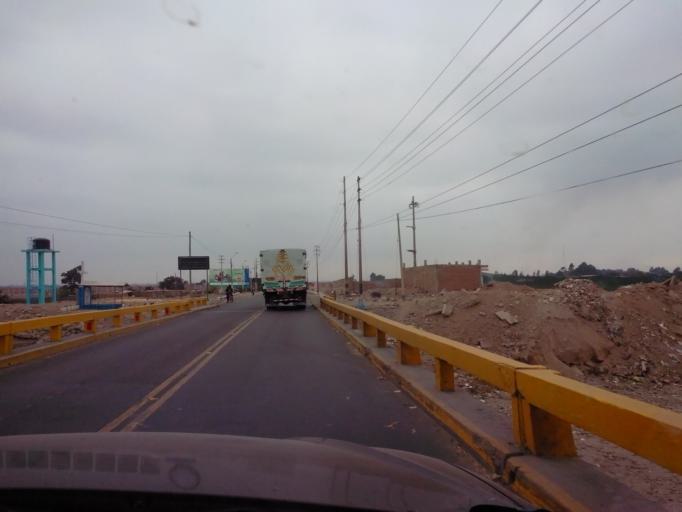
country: PE
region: Ica
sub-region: Provincia de Chincha
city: Chincha Baja
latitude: -13.4667
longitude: -76.1368
